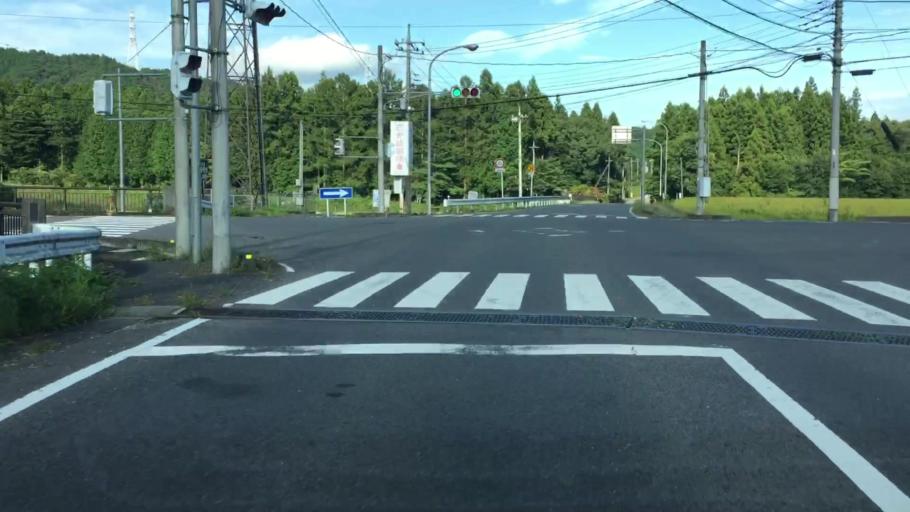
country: JP
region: Tochigi
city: Imaichi
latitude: 36.7649
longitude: 139.6755
